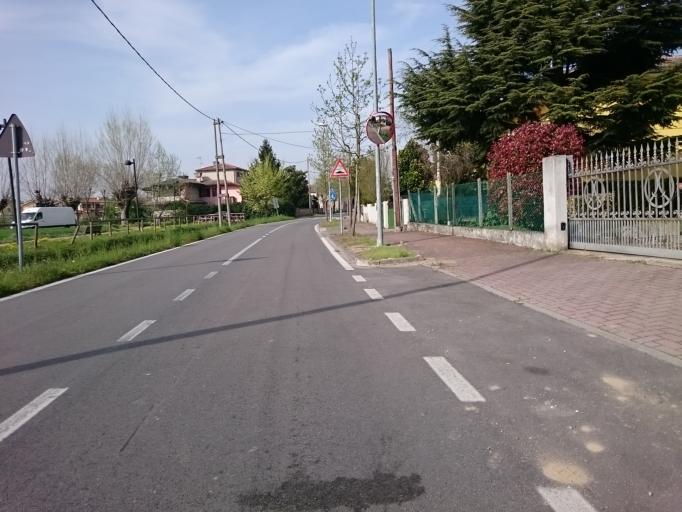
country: IT
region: Veneto
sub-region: Provincia di Padova
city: Masera di Padova
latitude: 45.3010
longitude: 11.8515
